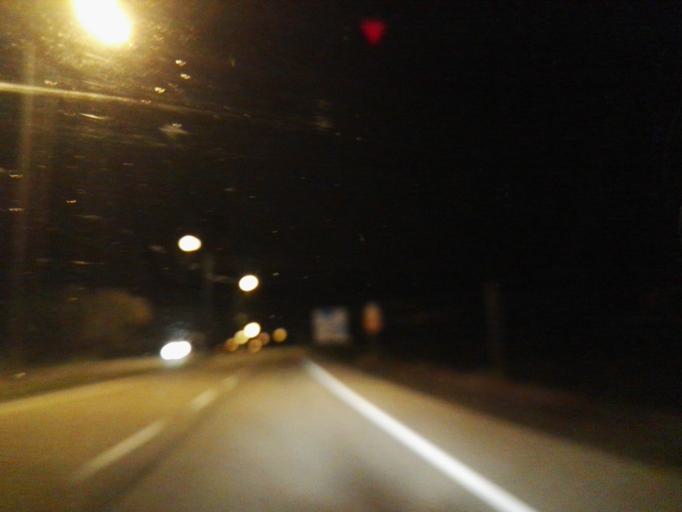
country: PT
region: Castelo Branco
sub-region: Castelo Branco
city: Castelo Branco
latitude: 39.8269
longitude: -7.5288
